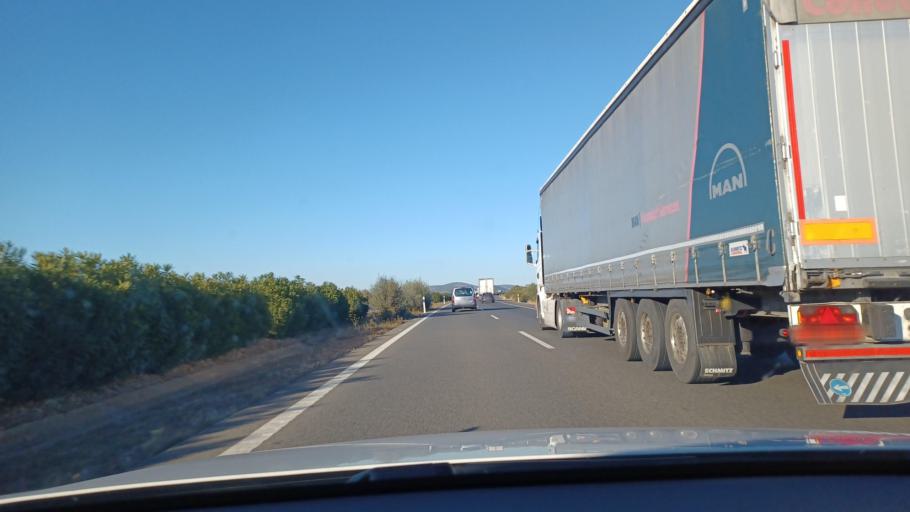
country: ES
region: Catalonia
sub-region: Provincia de Tarragona
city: Alcanar
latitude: 40.5421
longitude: 0.4189
